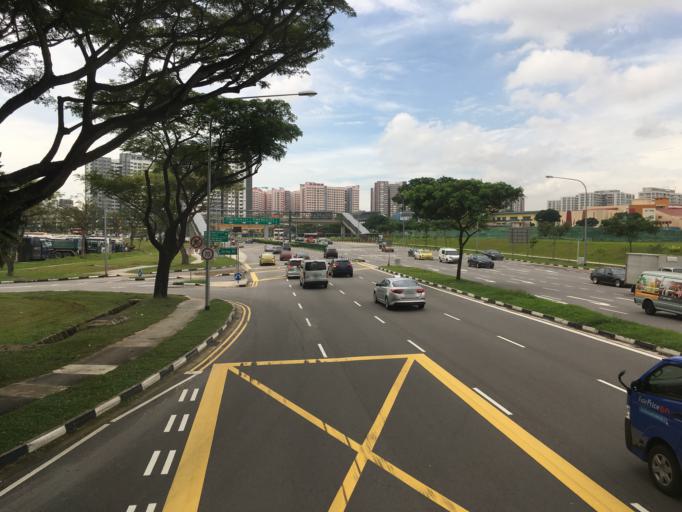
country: MY
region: Johor
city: Johor Bahru
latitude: 1.3466
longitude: 103.7375
